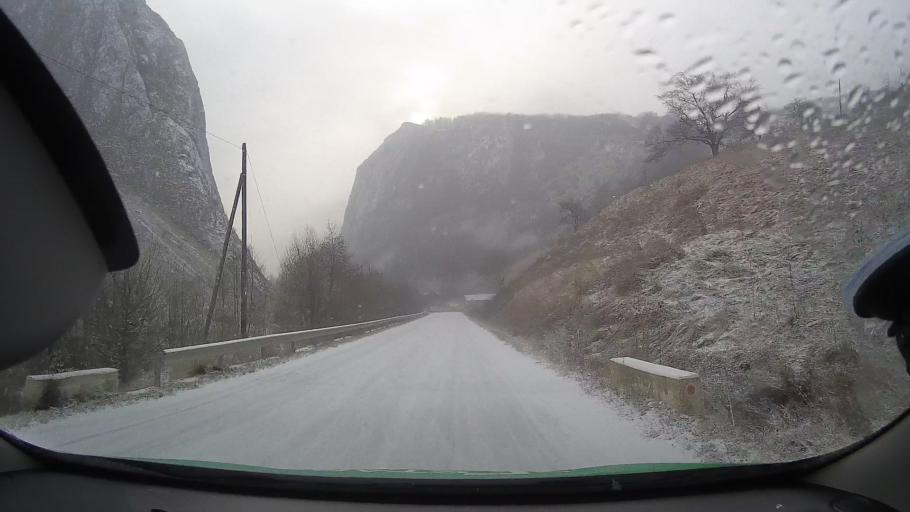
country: RO
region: Alba
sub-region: Comuna Livezile
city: Livezile
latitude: 46.3770
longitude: 23.5828
